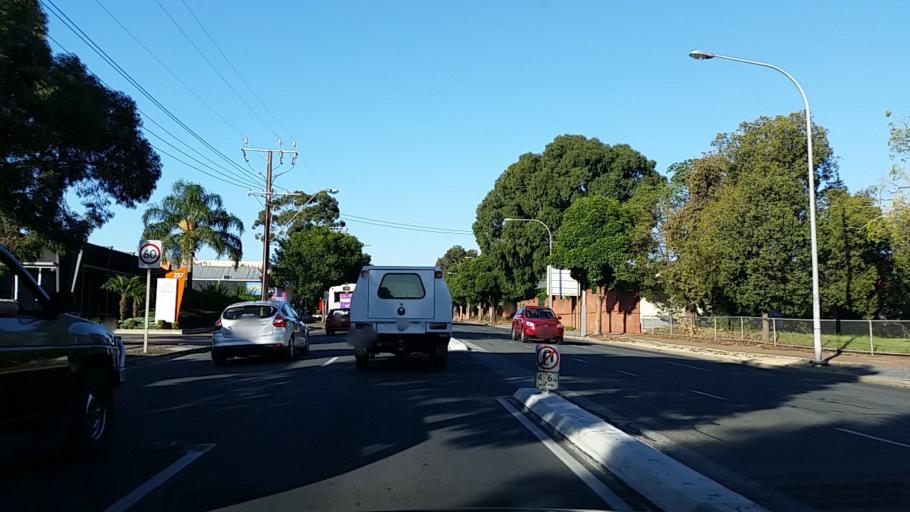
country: AU
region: South Australia
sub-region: Unley
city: Fullarton
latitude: -34.9400
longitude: 138.6263
